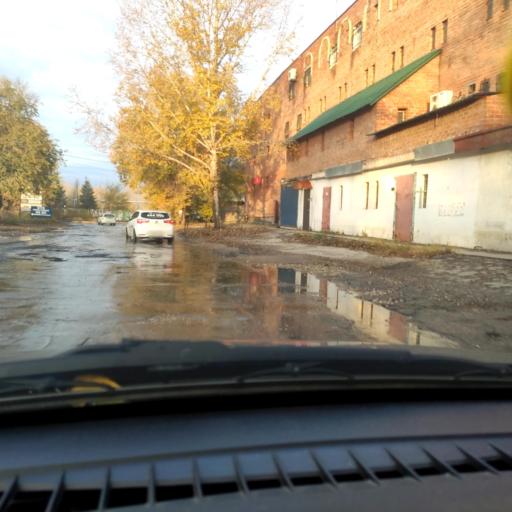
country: RU
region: Samara
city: Tol'yatti
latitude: 53.5384
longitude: 49.2895
